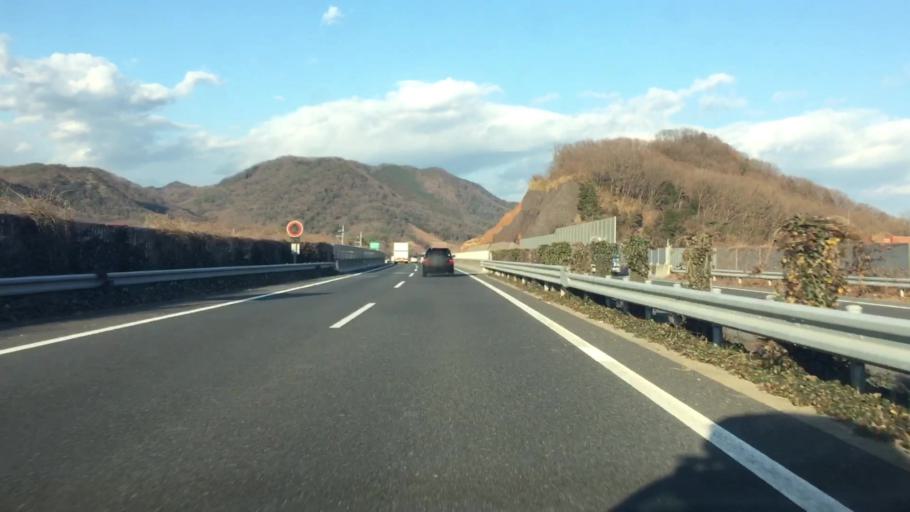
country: JP
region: Tochigi
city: Ashikaga
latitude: 36.3456
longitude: 139.4157
